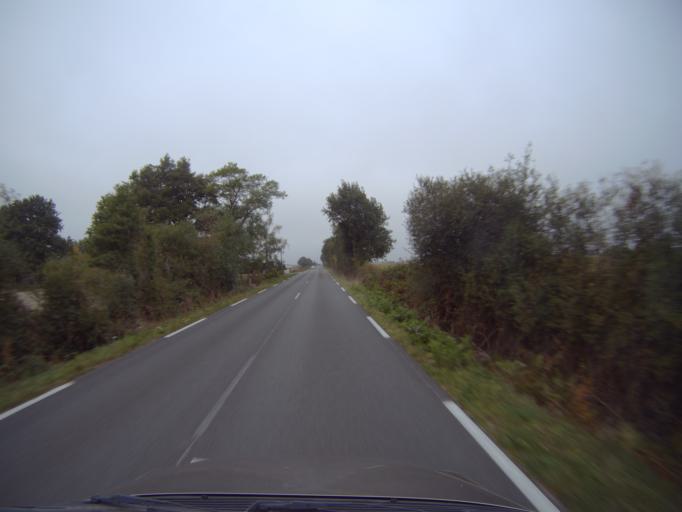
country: FR
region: Pays de la Loire
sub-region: Departement de la Vendee
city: Cugand
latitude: 47.0494
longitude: -1.2517
